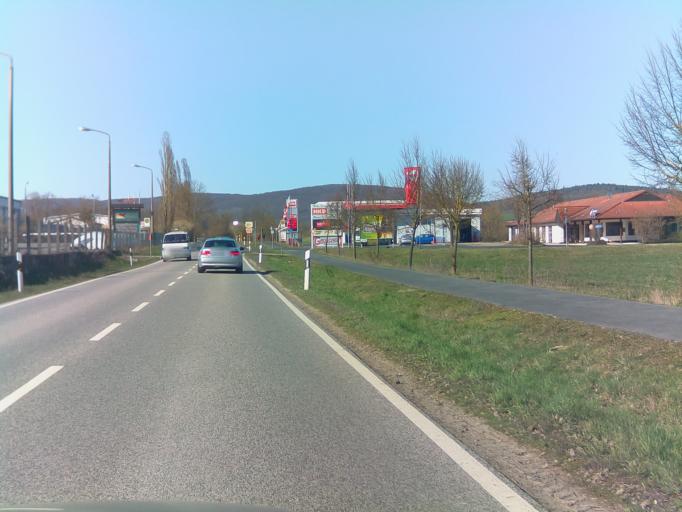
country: DE
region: Thuringia
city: Romhild
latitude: 50.4052
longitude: 10.5382
